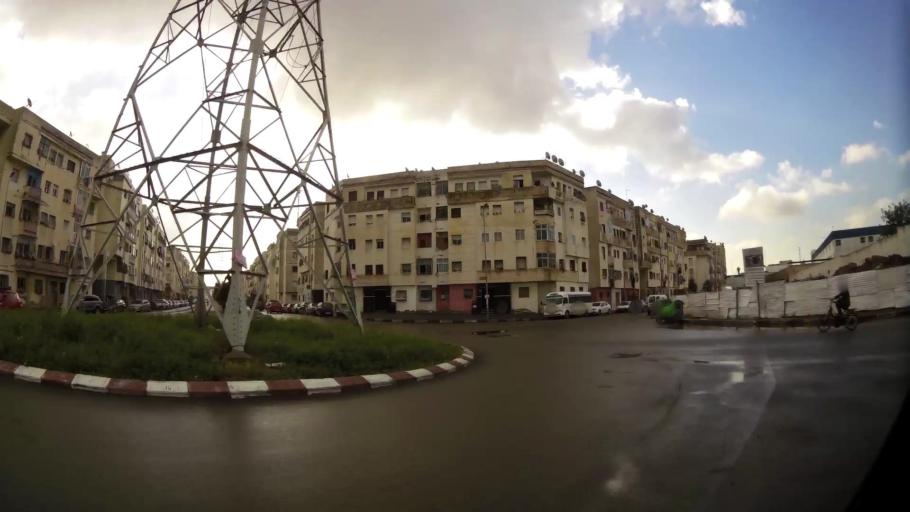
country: MA
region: Grand Casablanca
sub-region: Mediouna
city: Tit Mellil
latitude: 33.5922
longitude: -7.5399
